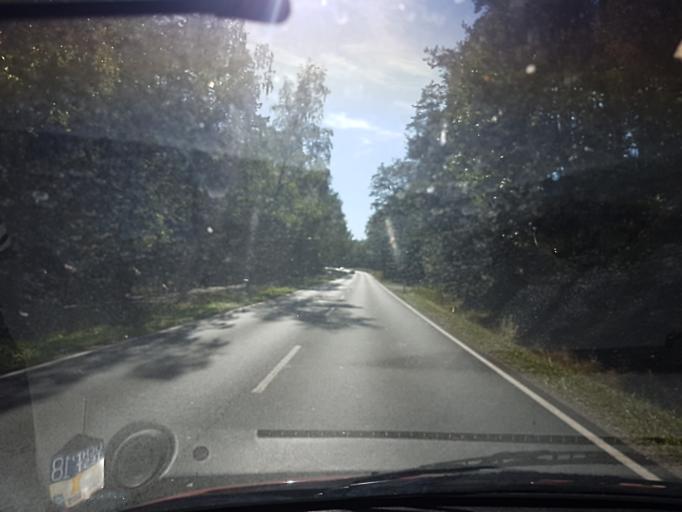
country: DE
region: Bavaria
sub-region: Regierungsbezirk Mittelfranken
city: Hemhofen
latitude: 49.7047
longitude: 10.9573
